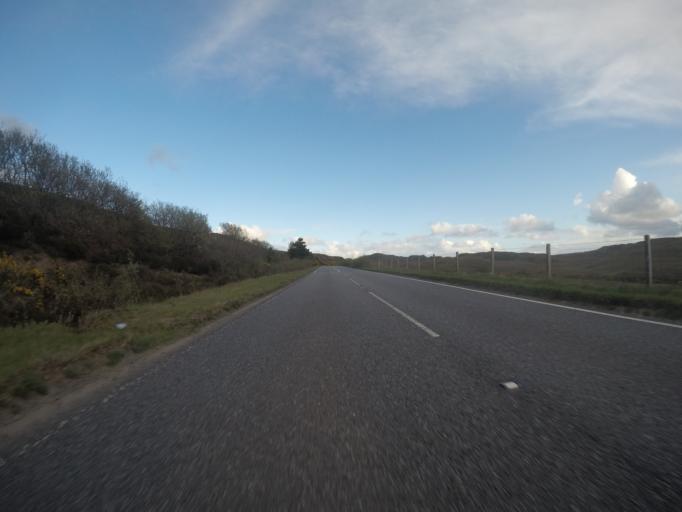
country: GB
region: Scotland
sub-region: Highland
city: Portree
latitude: 57.5242
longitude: -6.3440
